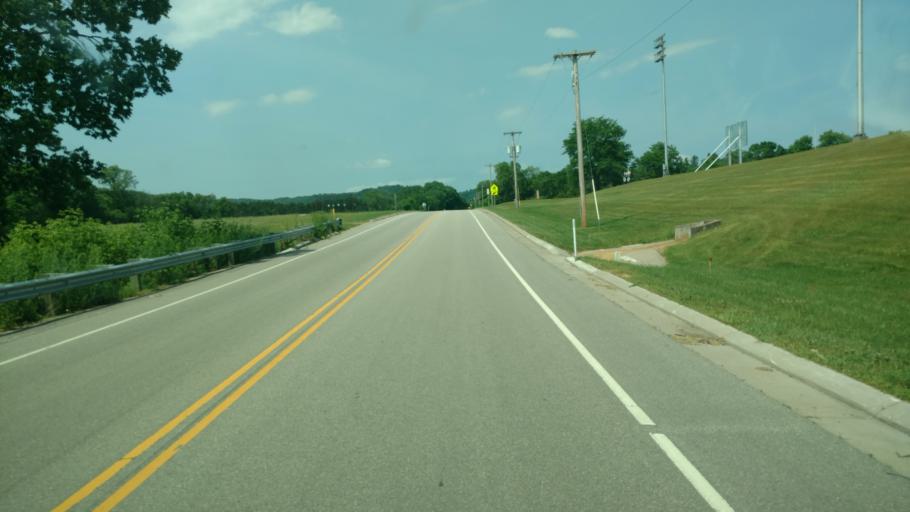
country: US
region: Wisconsin
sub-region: Vernon County
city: Viroqua
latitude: 43.4929
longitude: -90.6799
